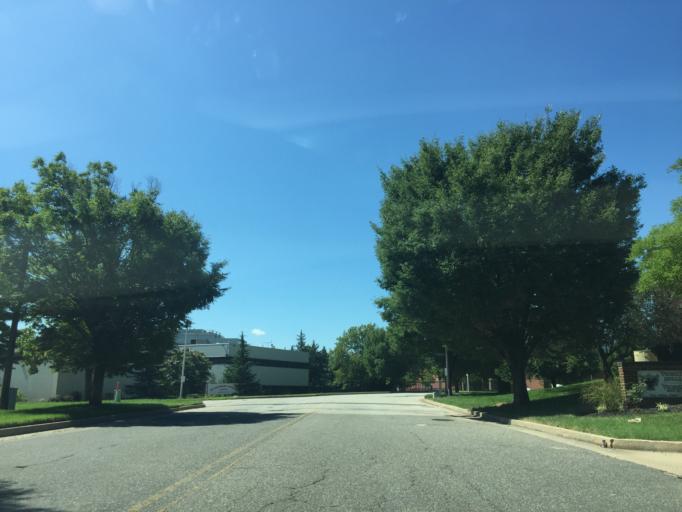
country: US
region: Maryland
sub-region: Baltimore County
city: Dundalk
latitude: 39.2685
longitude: -76.5323
